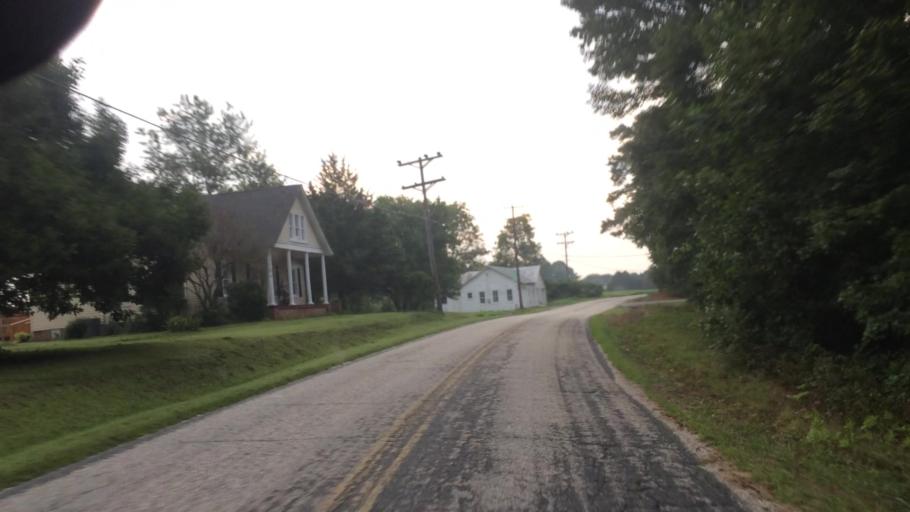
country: US
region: Virginia
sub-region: King William County
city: West Point
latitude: 37.5529
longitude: -76.7251
